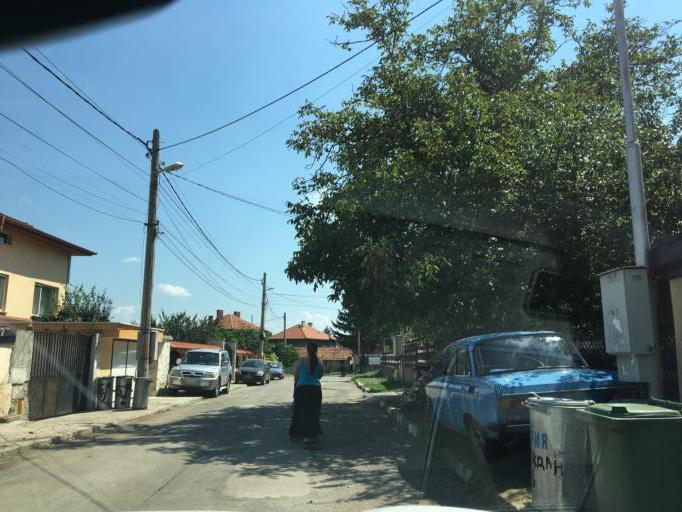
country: BG
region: Sofiya
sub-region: Obshtina Elin Pelin
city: Elin Pelin
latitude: 42.6050
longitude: 23.4707
